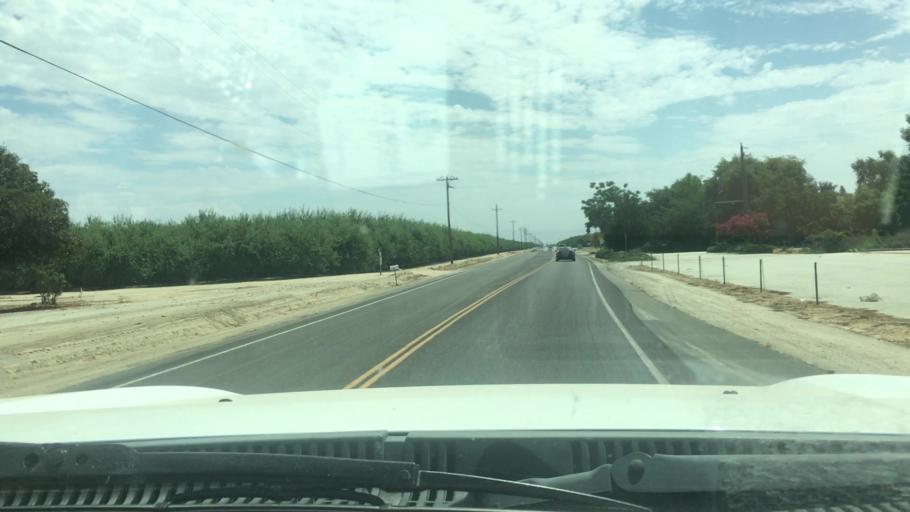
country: US
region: California
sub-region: Kern County
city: Wasco
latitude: 35.5580
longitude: -119.3271
